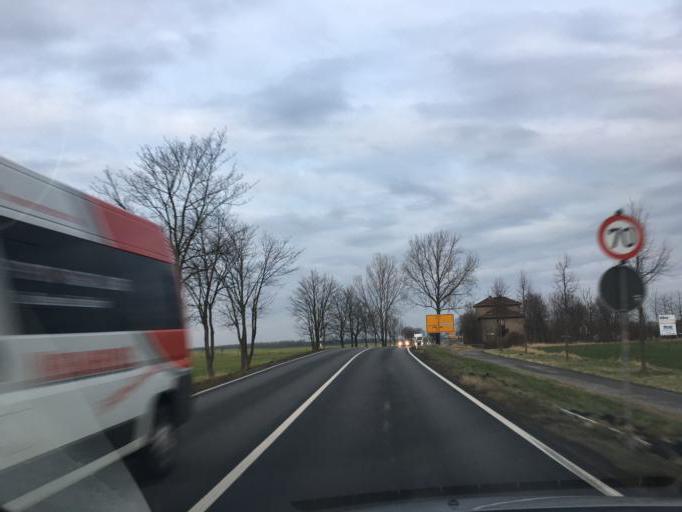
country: DE
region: Saxony
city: Regis-Breitingen
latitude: 51.0886
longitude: 12.4694
